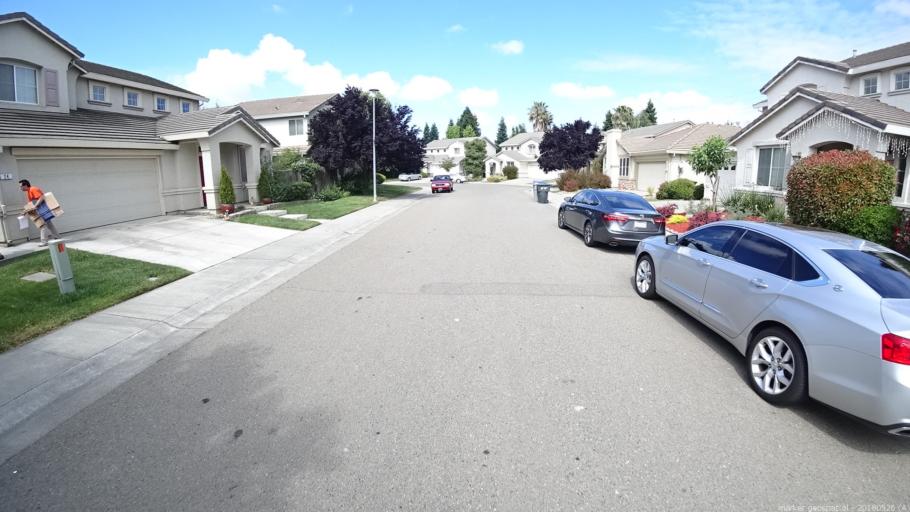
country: US
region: California
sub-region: Yolo County
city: West Sacramento
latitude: 38.6121
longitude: -121.5309
